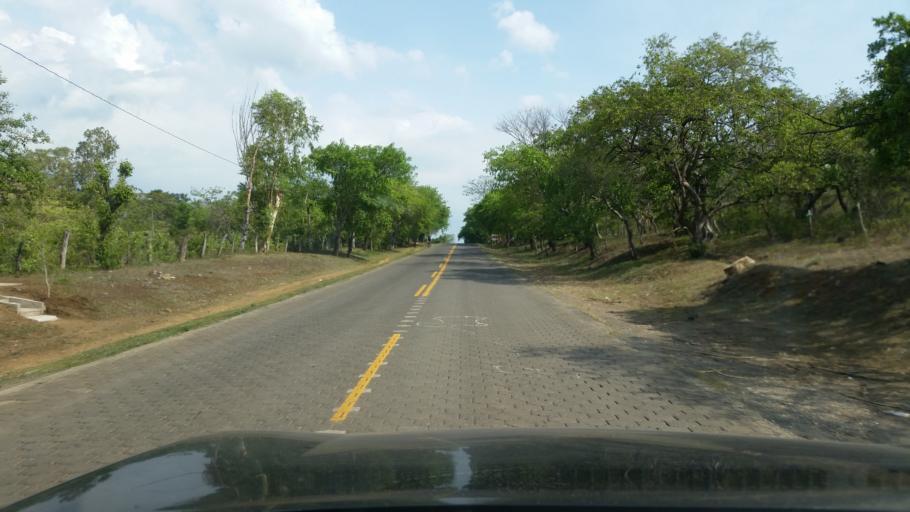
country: NI
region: Managua
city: Carlos Fonseca Amador
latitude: 11.9653
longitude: -86.5127
